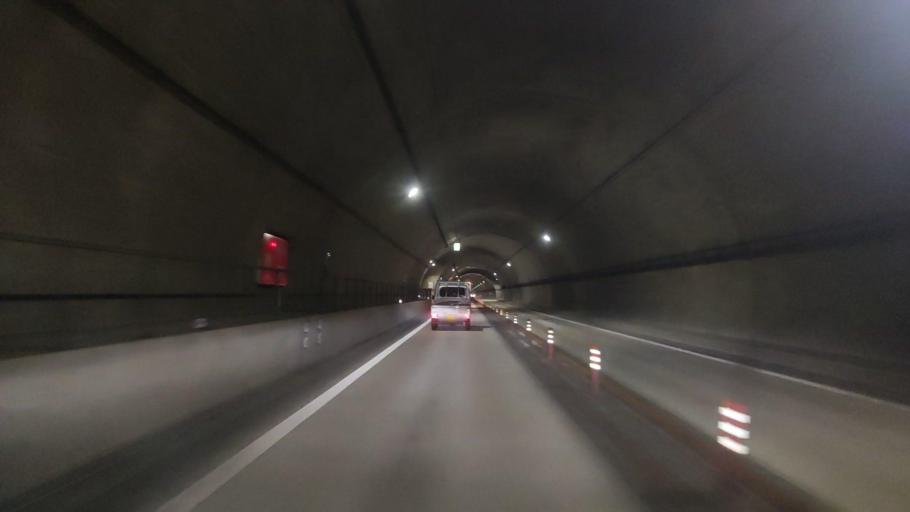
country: JP
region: Wakayama
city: Tanabe
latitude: 33.6153
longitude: 135.4232
